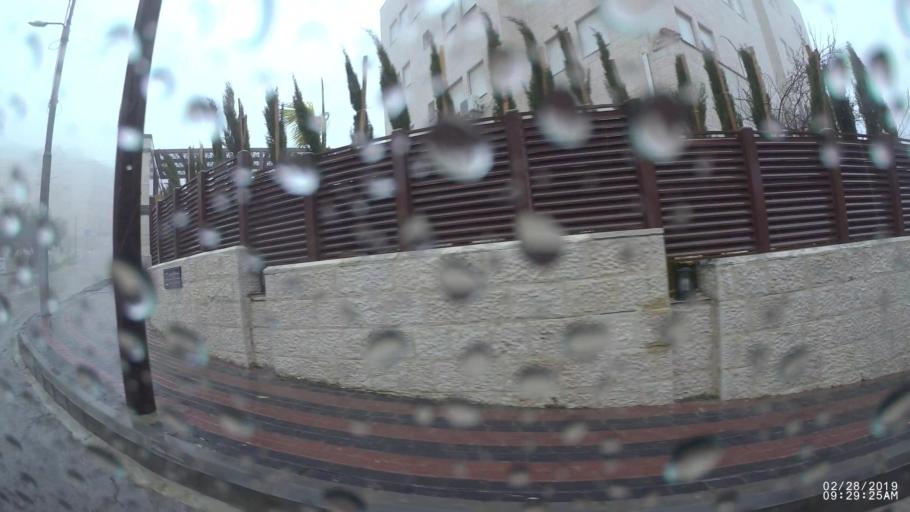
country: JO
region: Amman
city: Al Jubayhah
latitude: 32.0075
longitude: 35.8797
